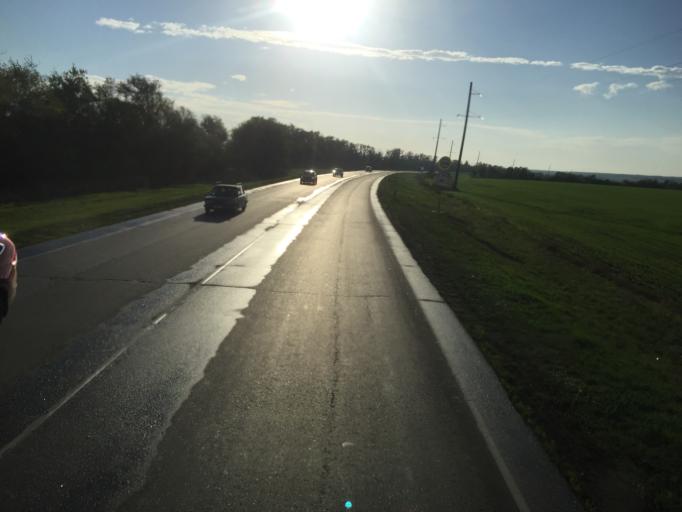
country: RU
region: Rostov
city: Mechetinskaya
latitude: 46.7884
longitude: 40.4043
